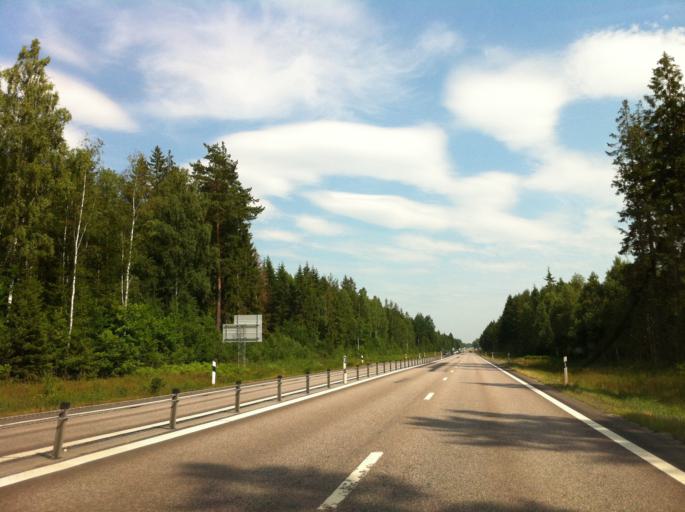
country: SE
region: Kalmar
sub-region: Kalmar Kommun
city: Trekanten
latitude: 56.7169
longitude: 16.0437
